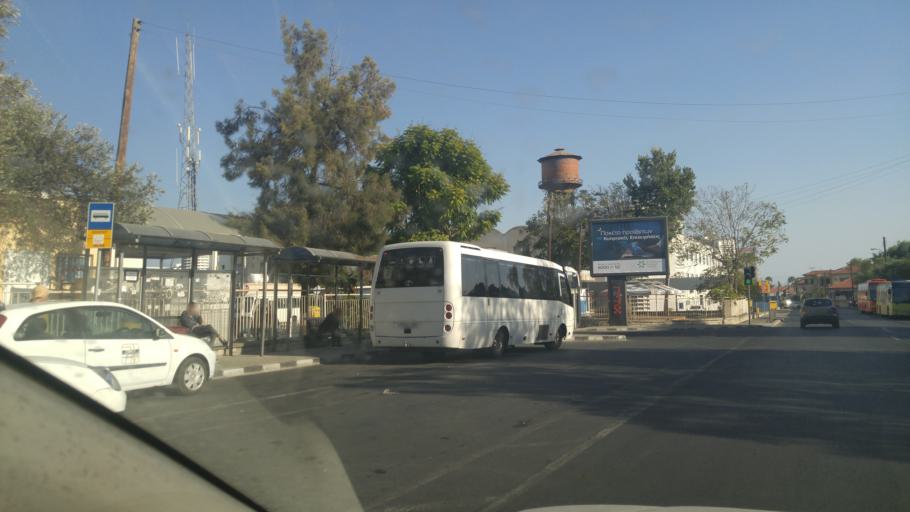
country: CY
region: Limassol
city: Limassol
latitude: 34.6792
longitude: 33.0369
